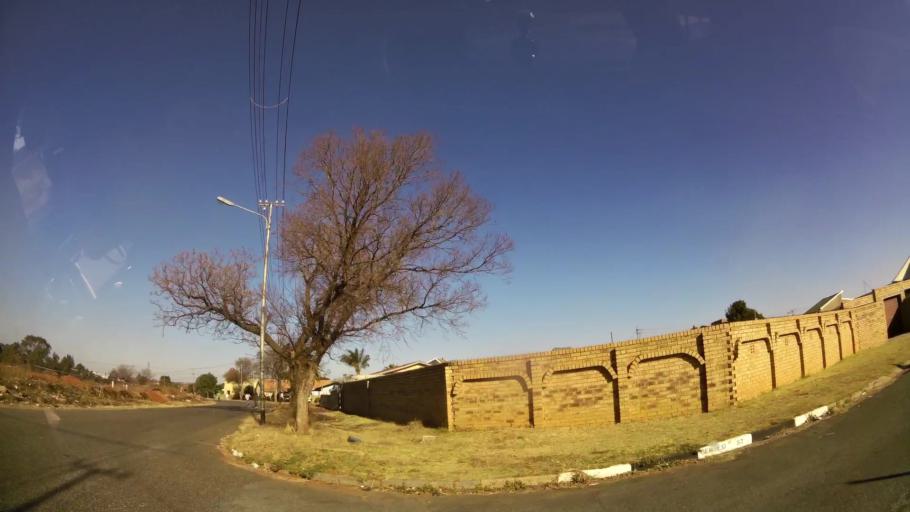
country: ZA
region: Gauteng
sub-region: City of Johannesburg Metropolitan Municipality
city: Johannesburg
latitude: -26.2125
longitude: 27.9824
